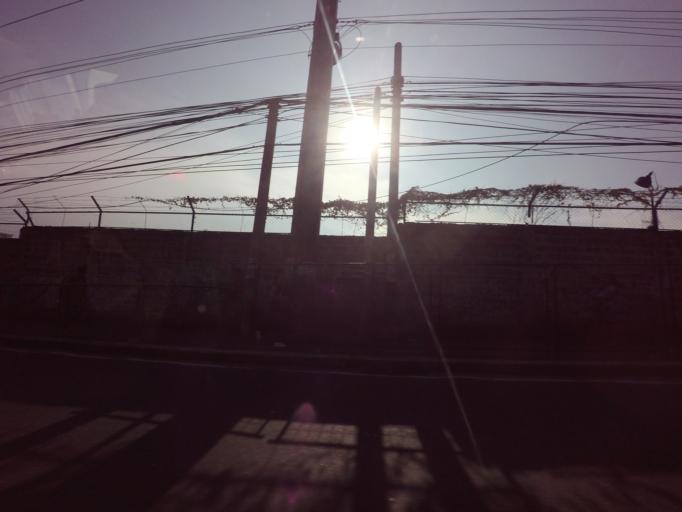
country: PH
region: Calabarzon
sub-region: Province of Rizal
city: Taguig
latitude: 14.4883
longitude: 121.0468
